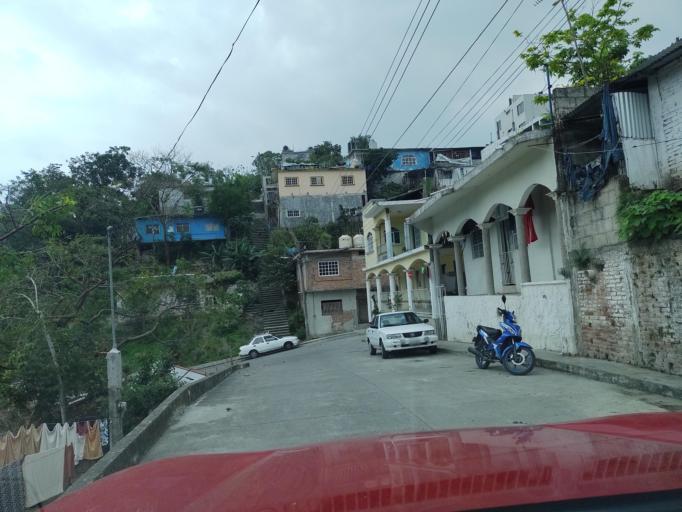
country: MX
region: Veracruz
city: Papantla de Olarte
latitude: 20.4592
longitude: -97.3307
